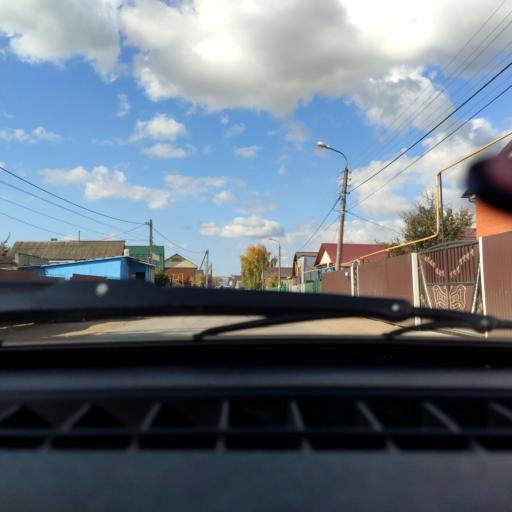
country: RU
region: Bashkortostan
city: Ufa
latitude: 54.7280
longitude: 55.9025
